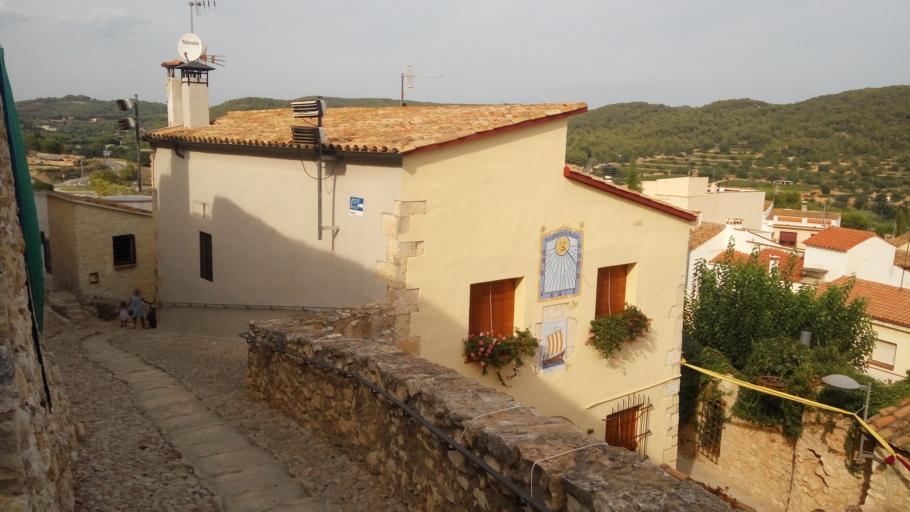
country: ES
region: Catalonia
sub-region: Provincia de Tarragona
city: Calafell
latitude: 41.2014
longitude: 1.5686
